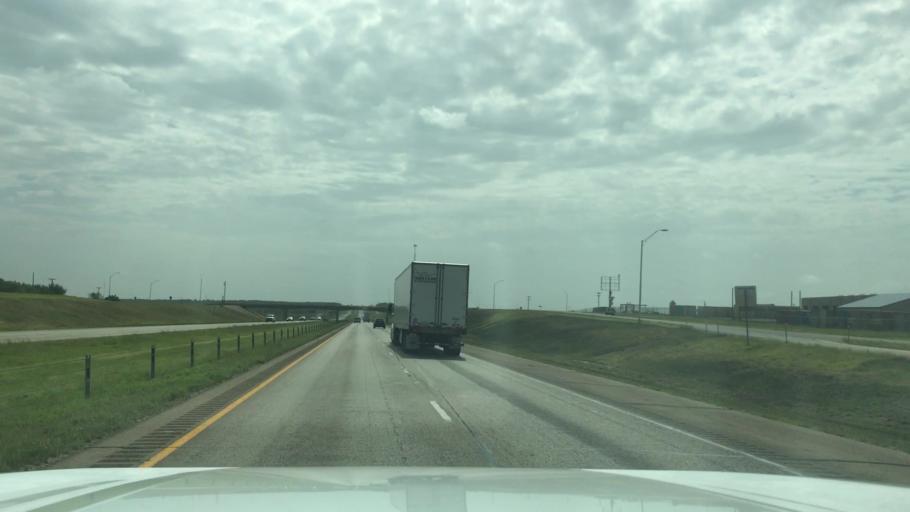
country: US
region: Texas
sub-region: Callahan County
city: Clyde
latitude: 32.4252
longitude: -99.5657
